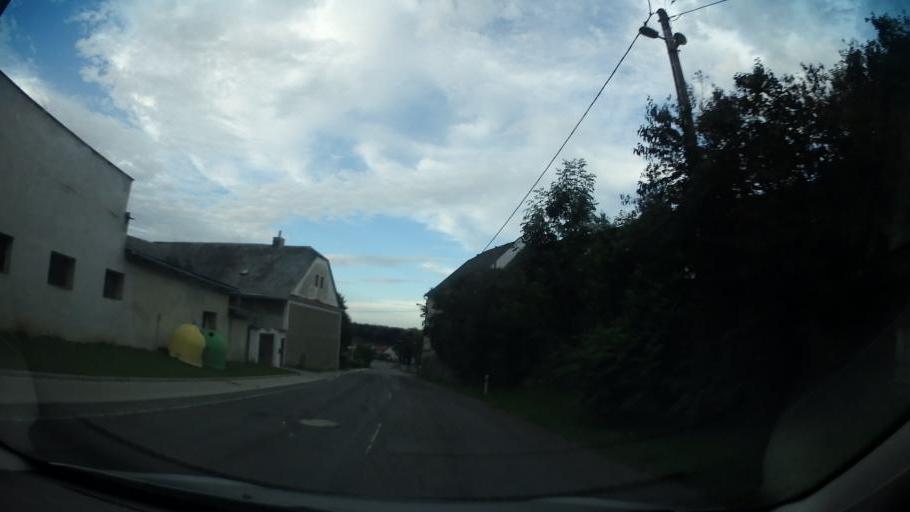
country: CZ
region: Olomoucky
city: Bila Lhota
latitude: 49.7044
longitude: 17.0176
